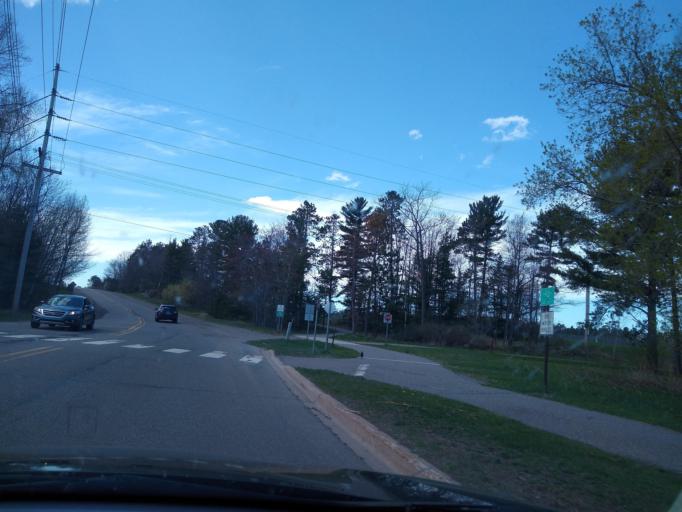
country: US
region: Michigan
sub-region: Marquette County
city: Marquette
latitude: 46.5714
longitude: -87.3998
